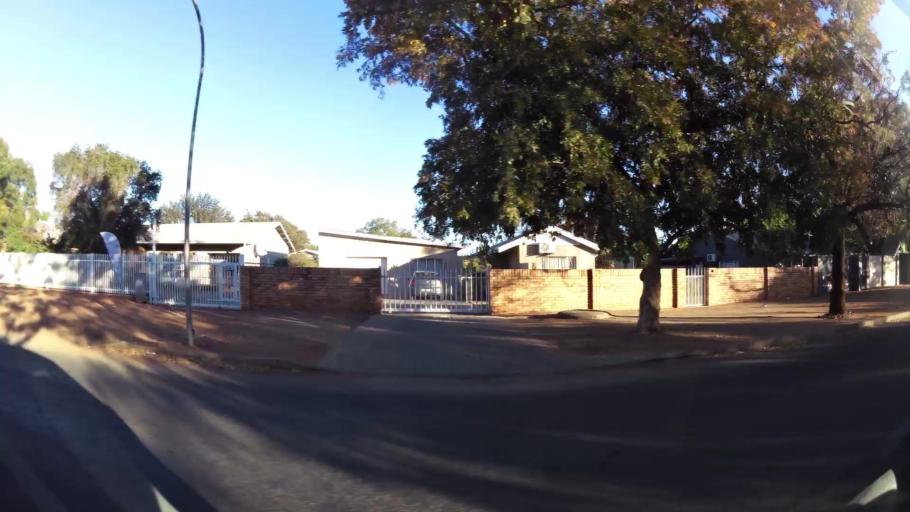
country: ZA
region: Northern Cape
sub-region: Frances Baard District Municipality
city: Kimberley
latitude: -28.7548
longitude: 24.7404
